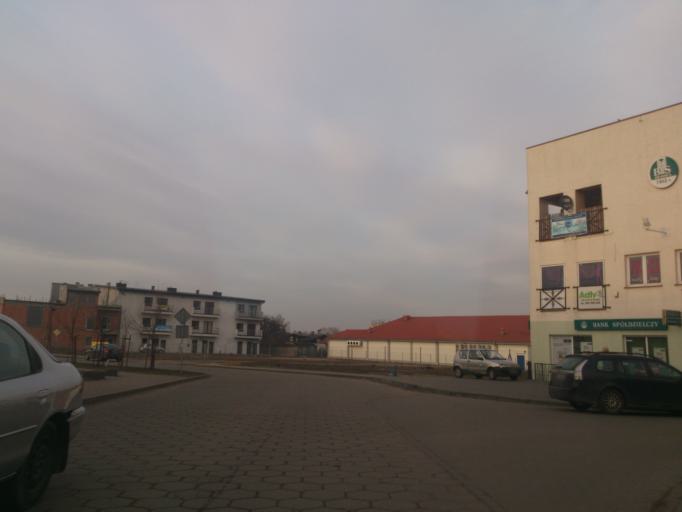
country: PL
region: Kujawsko-Pomorskie
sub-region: Powiat golubsko-dobrzynski
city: Golub-Dobrzyn
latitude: 53.1046
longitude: 19.0553
